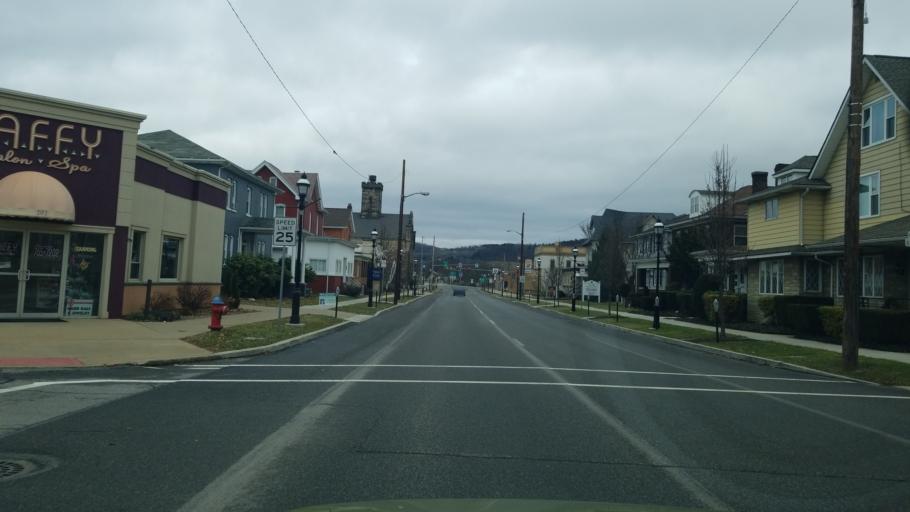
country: US
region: Pennsylvania
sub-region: Clearfield County
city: Clearfield
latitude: 41.0243
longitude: -78.4381
